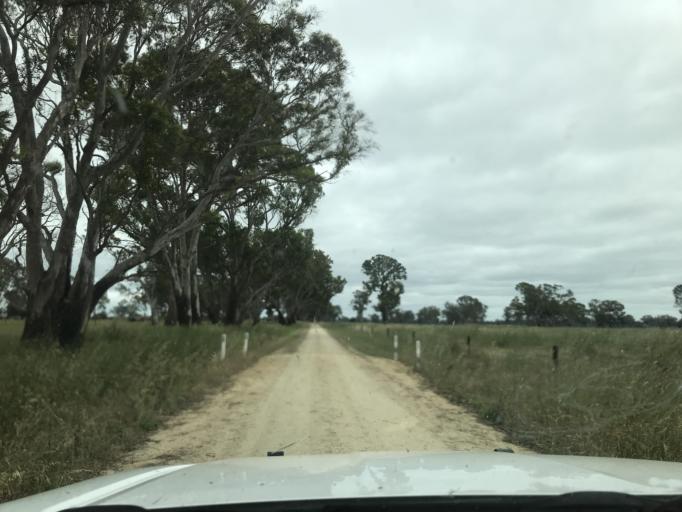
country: AU
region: South Australia
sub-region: Wattle Range
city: Penola
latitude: -37.1797
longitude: 141.0655
